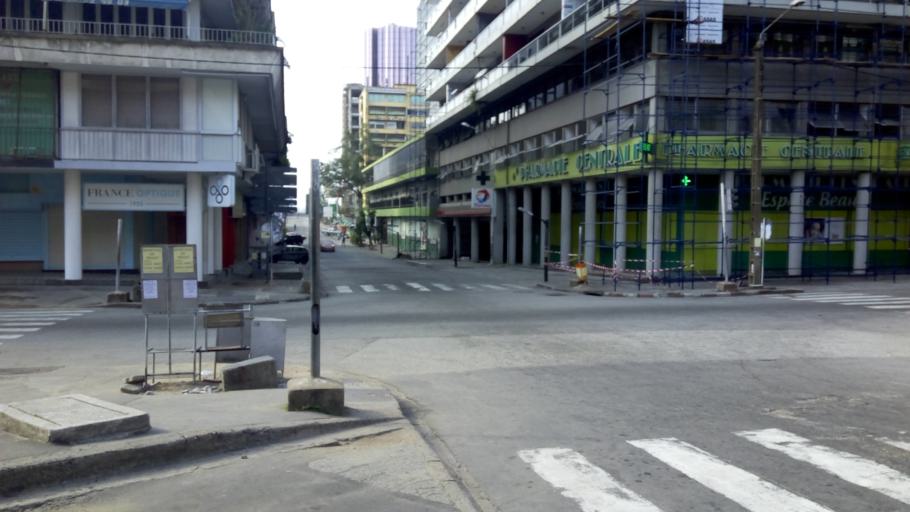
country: CI
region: Lagunes
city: Abidjan
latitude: 5.3217
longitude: -4.0181
